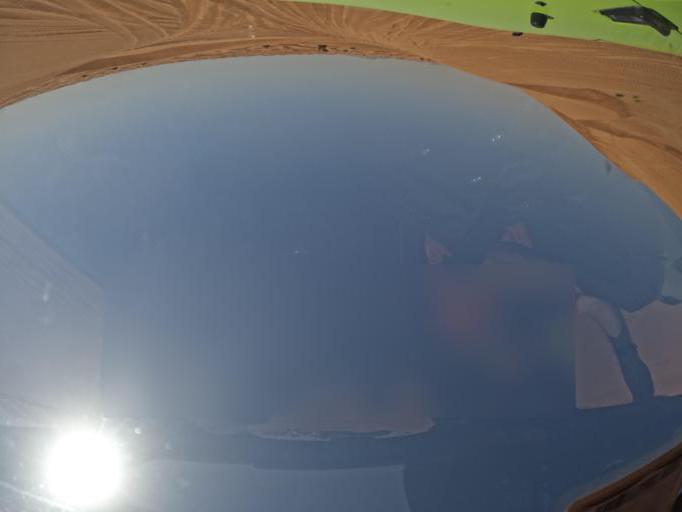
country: AE
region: Ash Shariqah
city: Adh Dhayd
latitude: 24.9572
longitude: 55.7184
